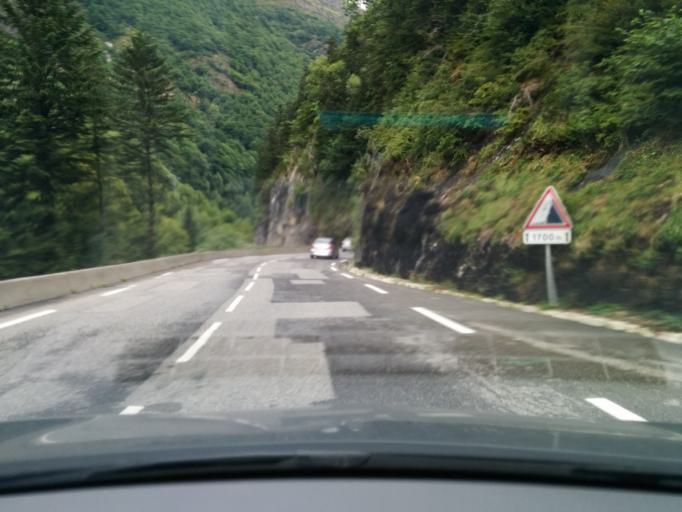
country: FR
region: Midi-Pyrenees
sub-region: Departement des Hautes-Pyrenees
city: Saint-Lary-Soulan
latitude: 42.7963
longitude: 0.2731
